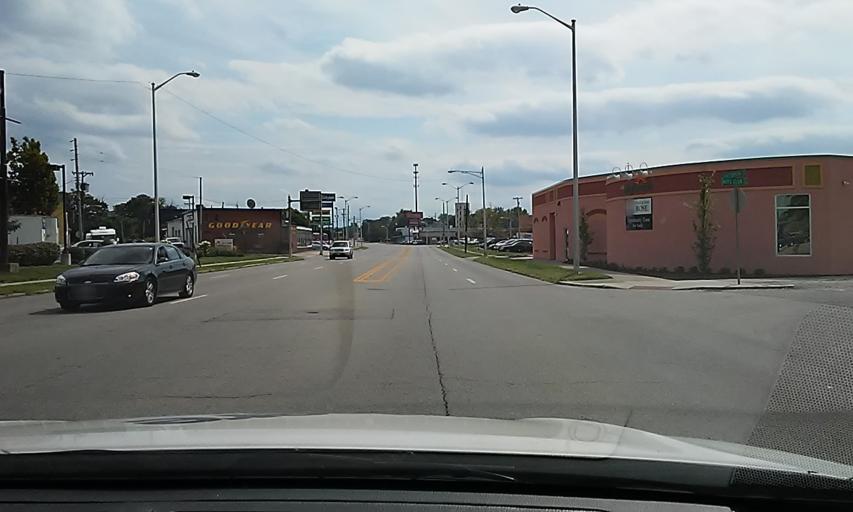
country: US
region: Ohio
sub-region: Montgomery County
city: Dayton
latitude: 39.7499
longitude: -84.1899
